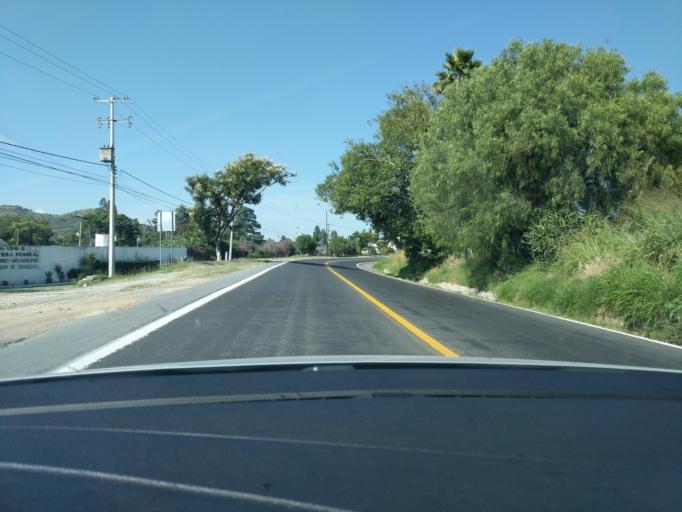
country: MX
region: Puebla
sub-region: Atlixco
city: San Agustin Huixaxtla
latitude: 18.9336
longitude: -98.4050
